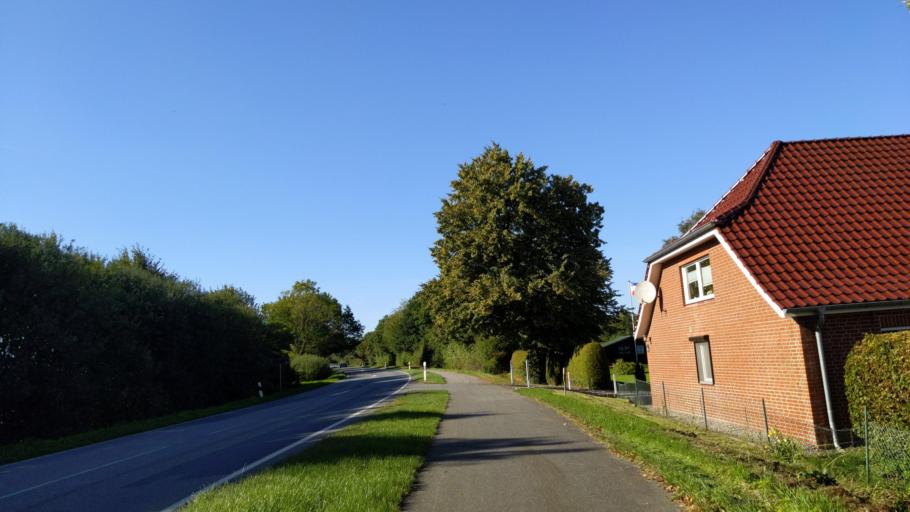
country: DE
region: Schleswig-Holstein
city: Ahrensbok
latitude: 53.9689
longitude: 10.5998
